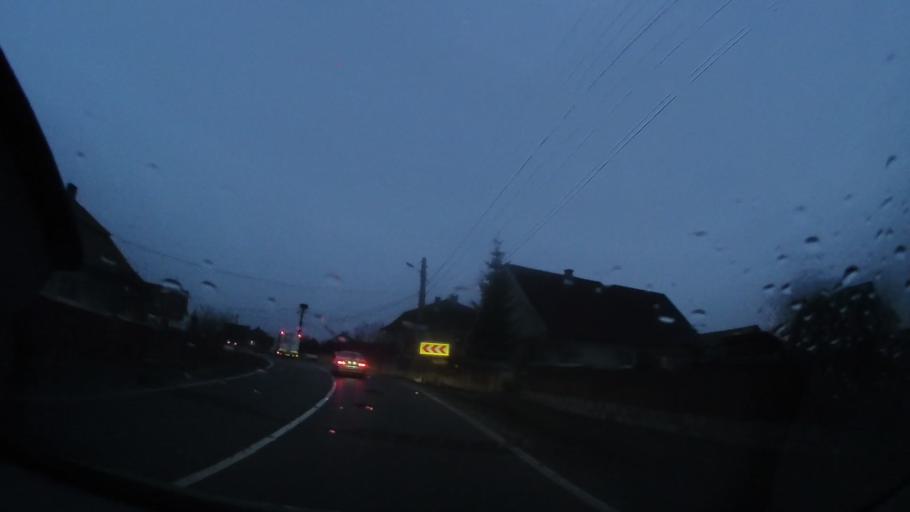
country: RO
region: Harghita
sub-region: Comuna Ditrau
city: Ditrau
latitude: 46.8124
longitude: 25.4940
